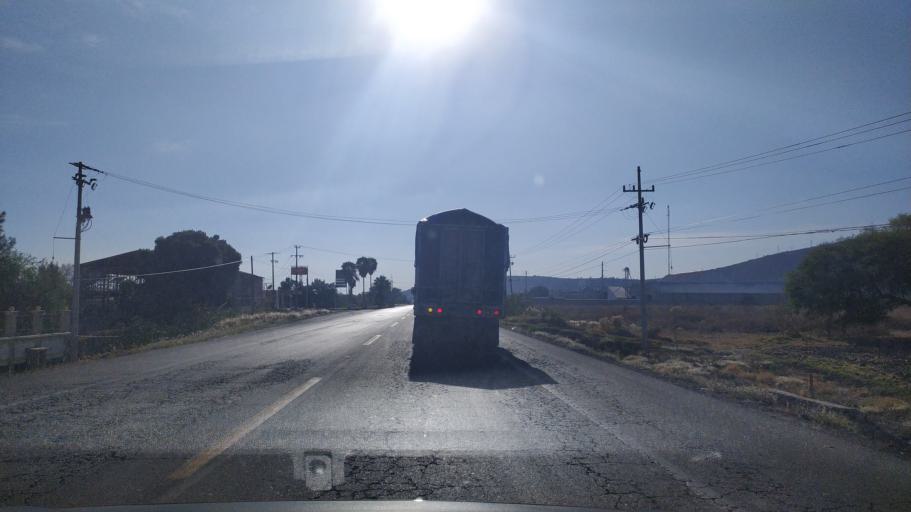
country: MX
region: Jalisco
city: Jamay
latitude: 20.2943
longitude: -102.6806
